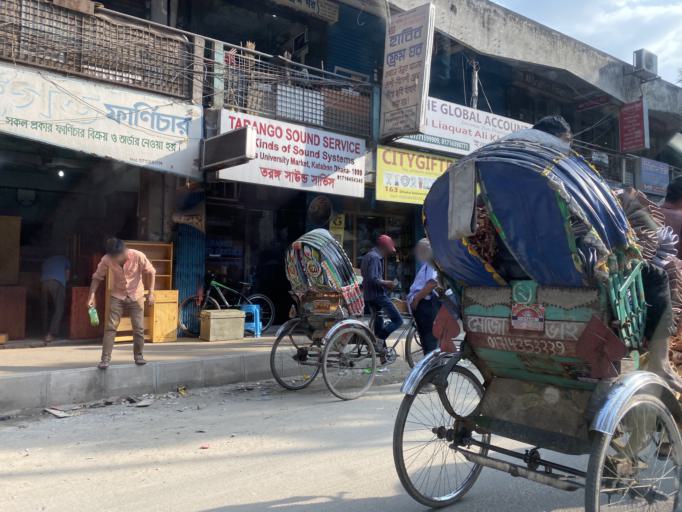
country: BD
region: Dhaka
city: Azimpur
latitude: 23.7347
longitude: 90.3881
